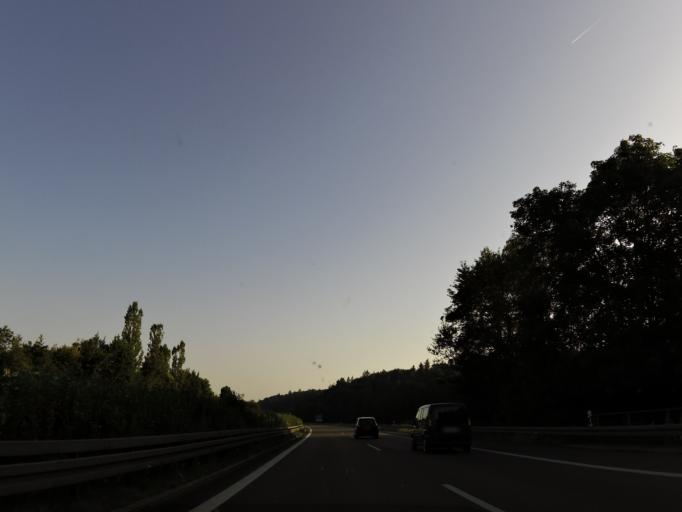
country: DE
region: Bavaria
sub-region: Swabia
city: Altenstadt
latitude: 48.1675
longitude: 10.1321
